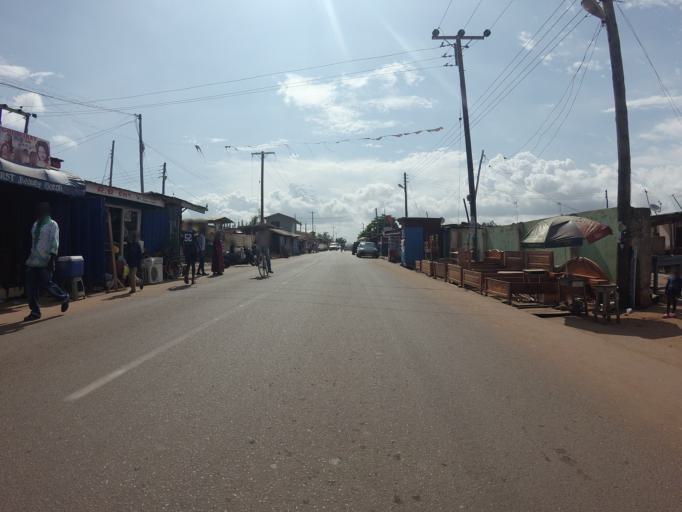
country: GH
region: Greater Accra
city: Medina Estates
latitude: 5.6789
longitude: -0.1777
